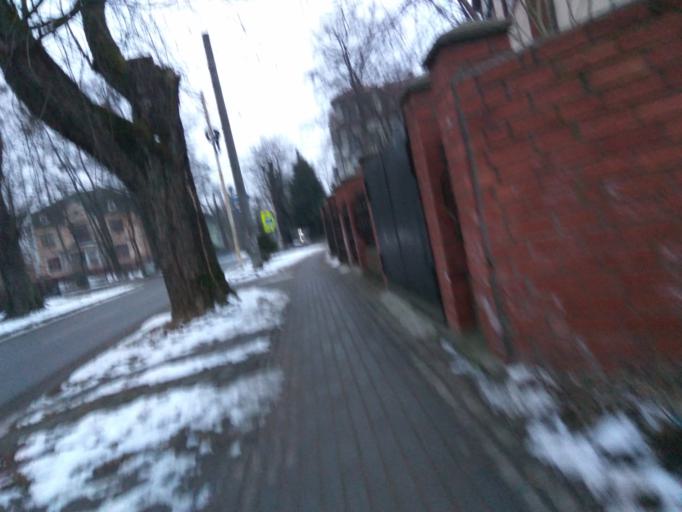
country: RU
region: Kaliningrad
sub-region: Gorod Kaliningrad
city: Kaliningrad
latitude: 54.7164
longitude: 20.4693
